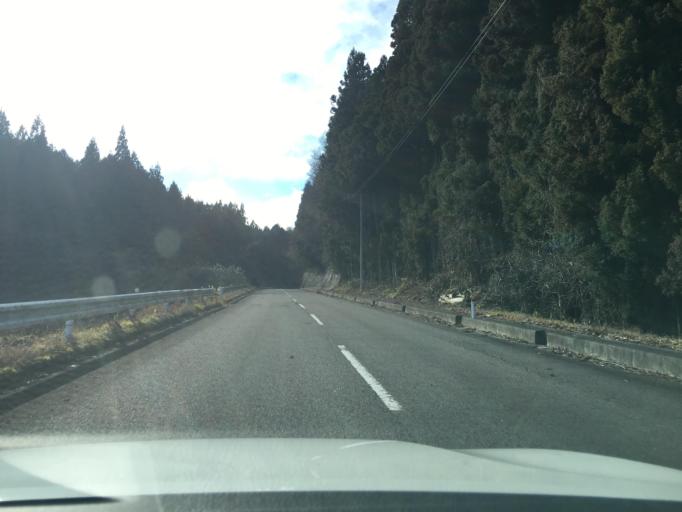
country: JP
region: Fukushima
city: Funehikimachi-funehiki
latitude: 37.3660
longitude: 140.6264
